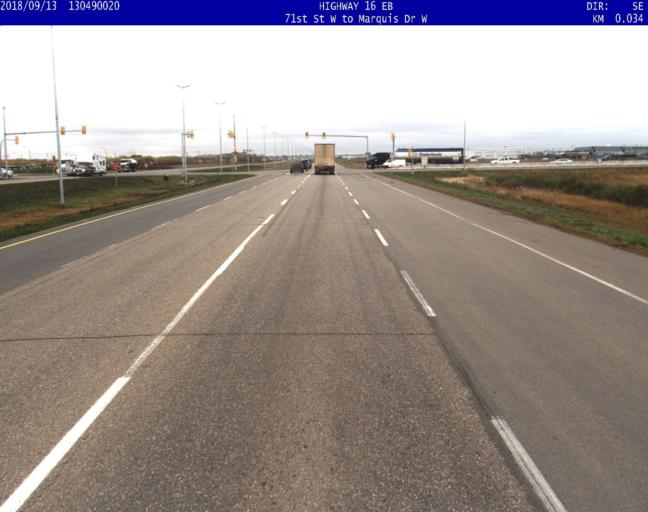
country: CA
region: Saskatchewan
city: Martensville
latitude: 52.2019
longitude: -106.7046
